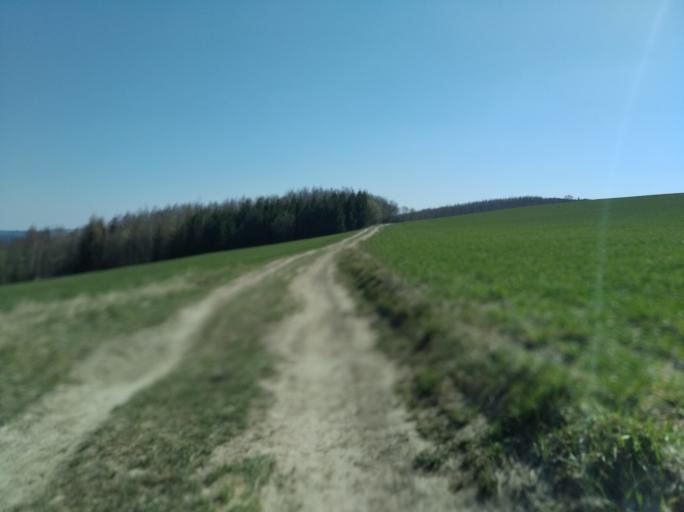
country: PL
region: Subcarpathian Voivodeship
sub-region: Powiat strzyzowski
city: Polomia
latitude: 49.8834
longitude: 21.8526
